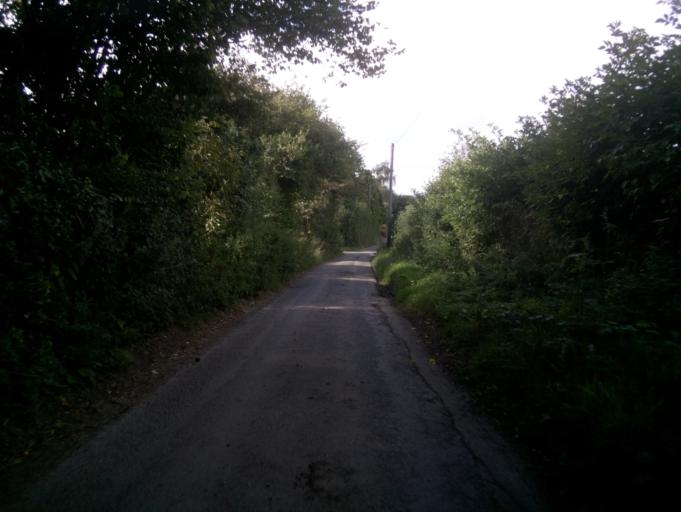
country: GB
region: England
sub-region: Gloucestershire
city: Painswick
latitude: 51.7894
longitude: -2.2432
